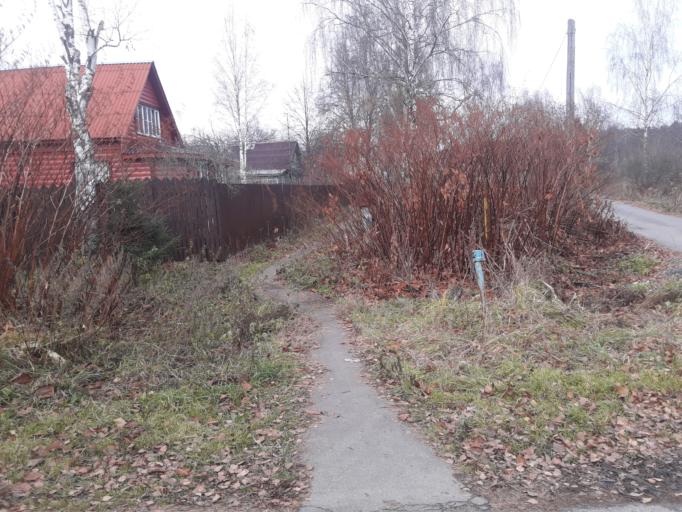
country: RU
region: Moskovskaya
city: Ashukino
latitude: 56.1661
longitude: 37.9632
